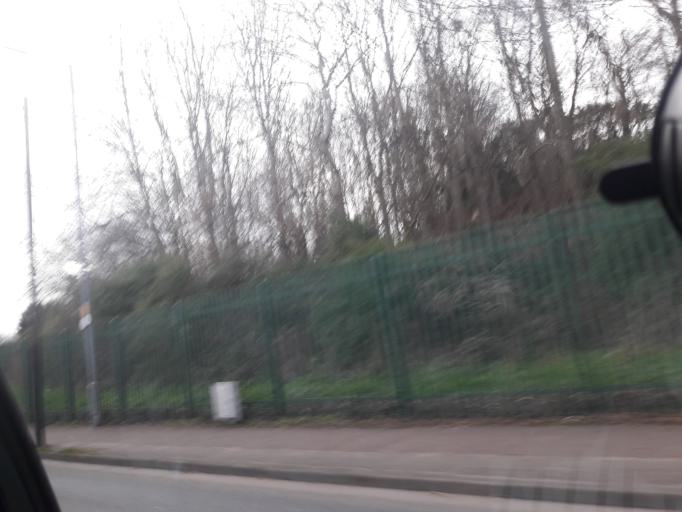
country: GB
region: Northern Ireland
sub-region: City of Belfast
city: Belfast
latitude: 54.6241
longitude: -5.9492
